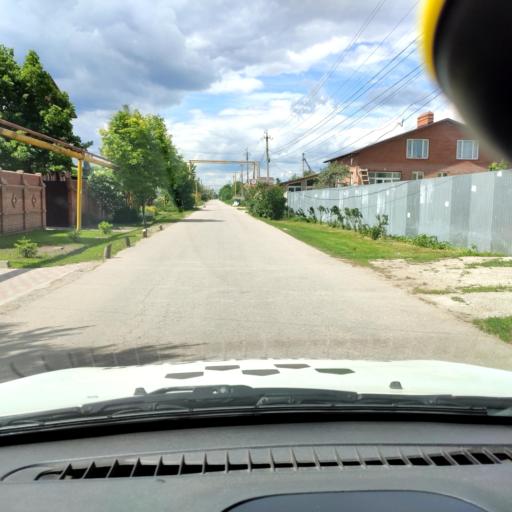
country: RU
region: Samara
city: Podstepki
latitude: 53.5165
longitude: 49.1680
